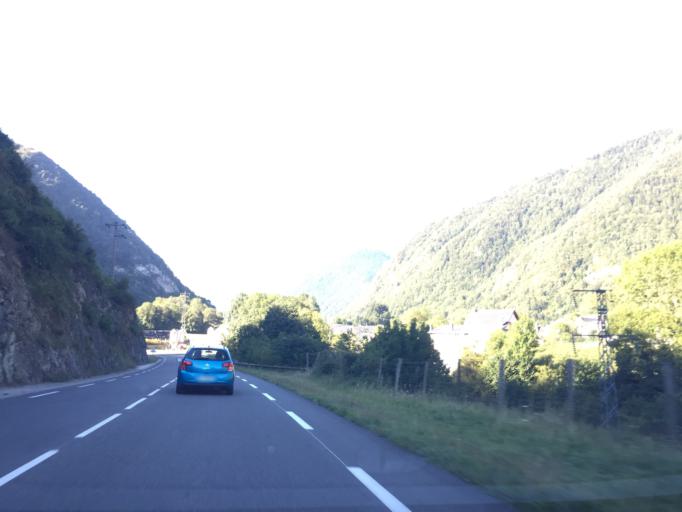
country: FR
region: Midi-Pyrenees
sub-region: Departement des Hautes-Pyrenees
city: Saint-Lary-Soulan
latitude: 42.8921
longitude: 0.3529
